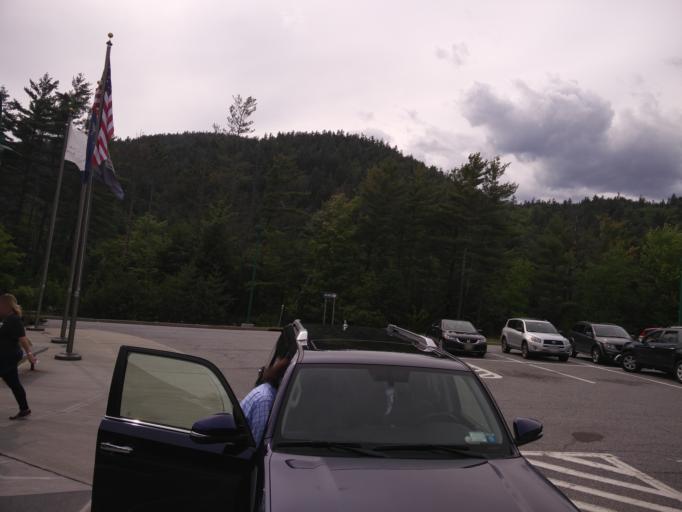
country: US
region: New York
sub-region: Essex County
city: Mineville
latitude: 44.0138
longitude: -73.7051
